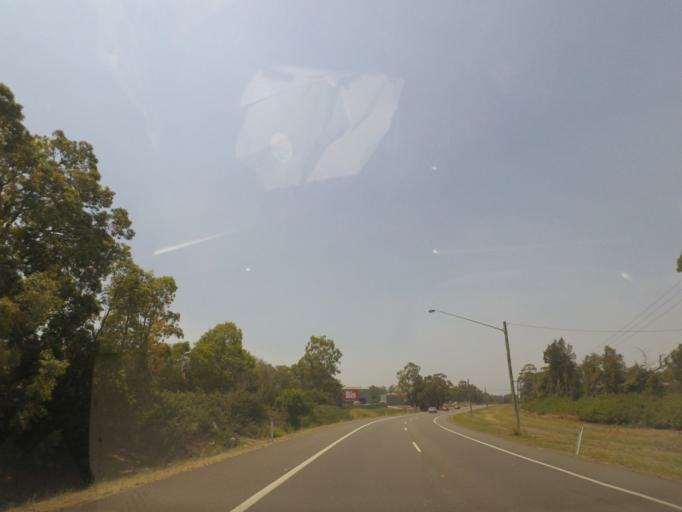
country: AU
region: New South Wales
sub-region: Newcastle
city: Beresfield
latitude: -32.8240
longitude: 151.7063
